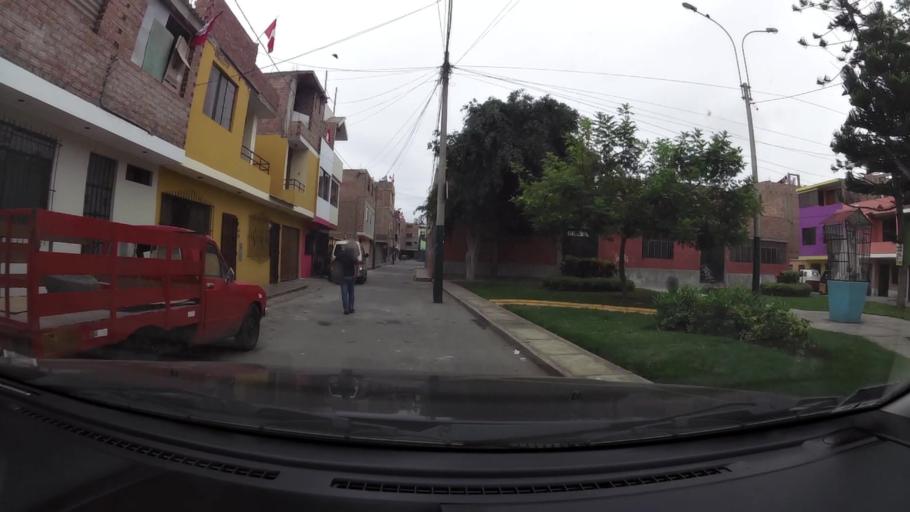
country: PE
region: Lima
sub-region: Lima
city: Surco
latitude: -12.1533
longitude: -77.0166
